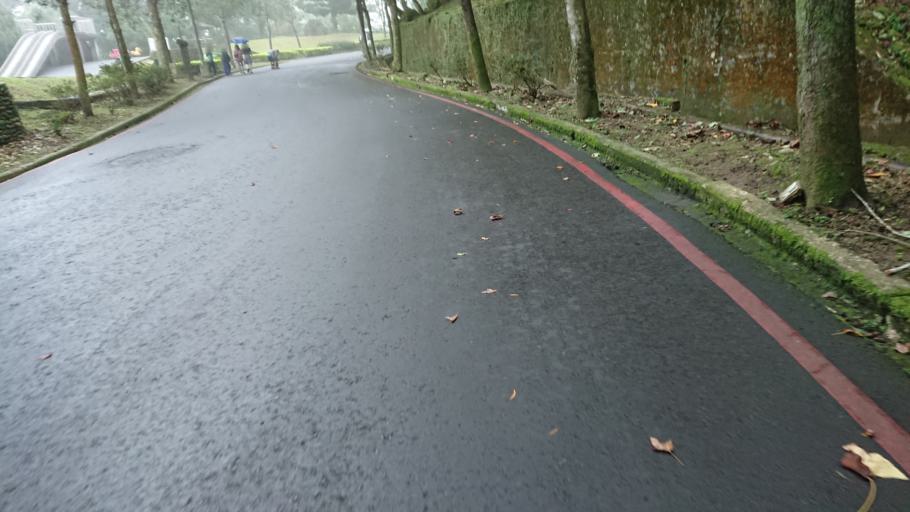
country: TW
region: Taiwan
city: Daxi
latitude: 24.8164
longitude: 121.2411
